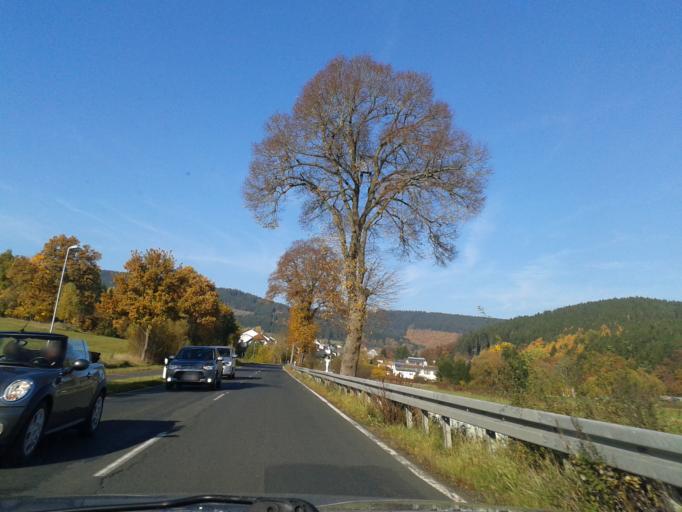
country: DE
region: Hesse
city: Dillenburg
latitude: 50.8445
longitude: 8.3408
